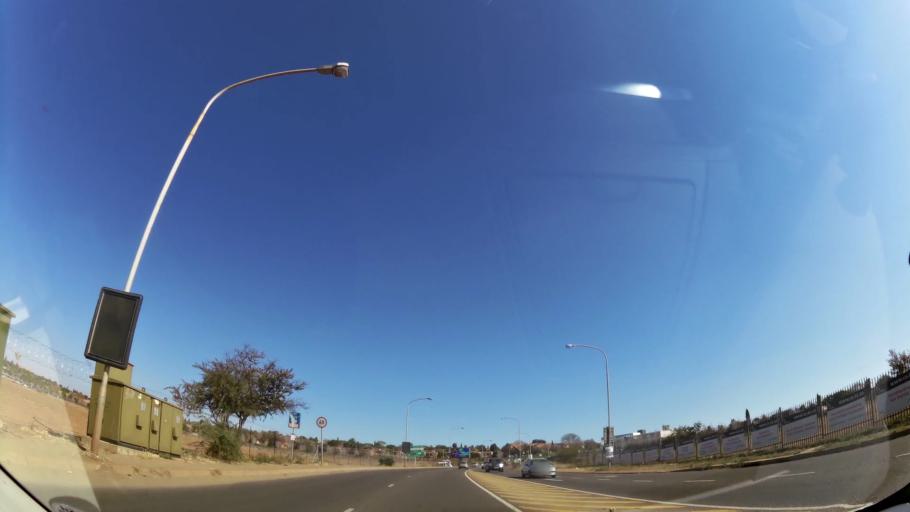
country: ZA
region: Gauteng
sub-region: City of Tshwane Metropolitan Municipality
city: Centurion
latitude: -25.8576
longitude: 28.1823
